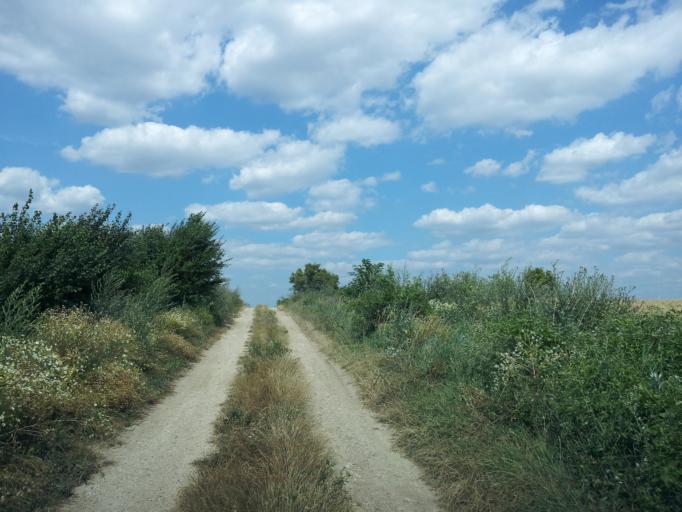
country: HU
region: Veszprem
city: Balatonkenese
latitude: 47.0539
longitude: 18.0773
